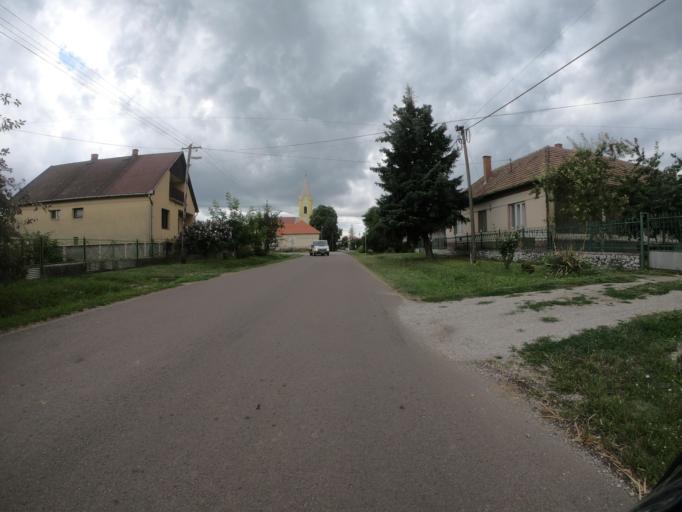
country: HU
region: Heves
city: Poroszlo
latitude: 47.7013
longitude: 20.6998
